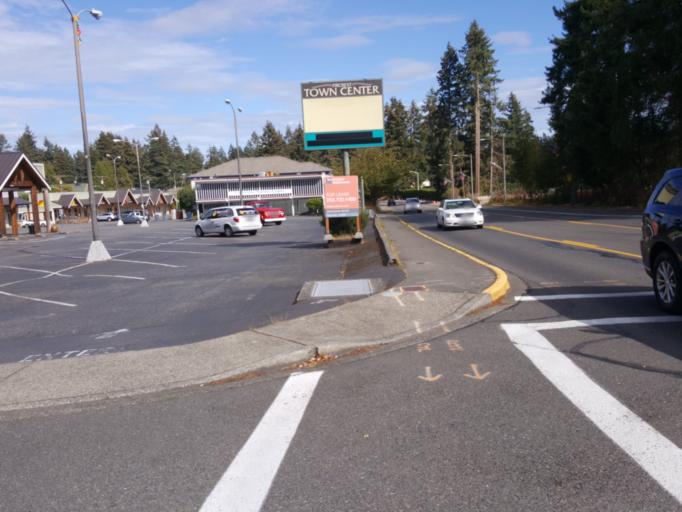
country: US
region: Washington
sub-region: Pierce County
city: Fircrest
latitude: 47.2389
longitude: -122.5199
